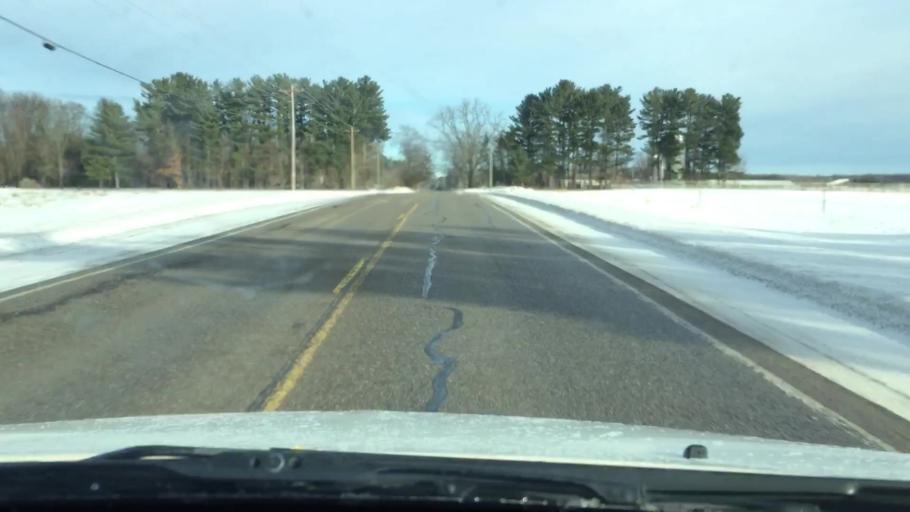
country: US
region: Michigan
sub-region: Kalkaska County
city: Kalkaska
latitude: 44.6410
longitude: -85.2609
